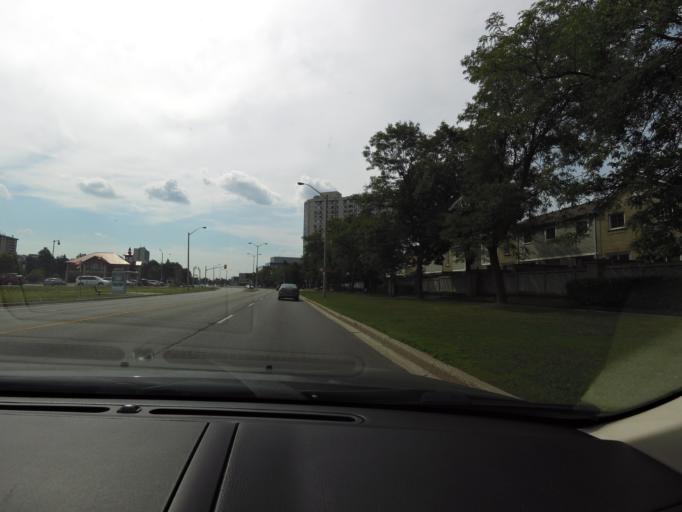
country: CA
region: Ontario
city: Brampton
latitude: 43.7225
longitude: -79.7247
